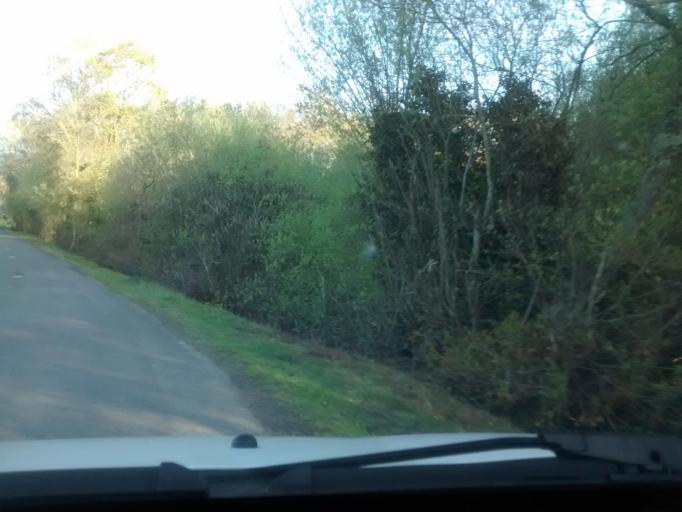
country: FR
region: Brittany
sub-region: Departement d'Ille-et-Vilaine
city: Saint-Broladre
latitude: 48.5558
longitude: -1.6290
